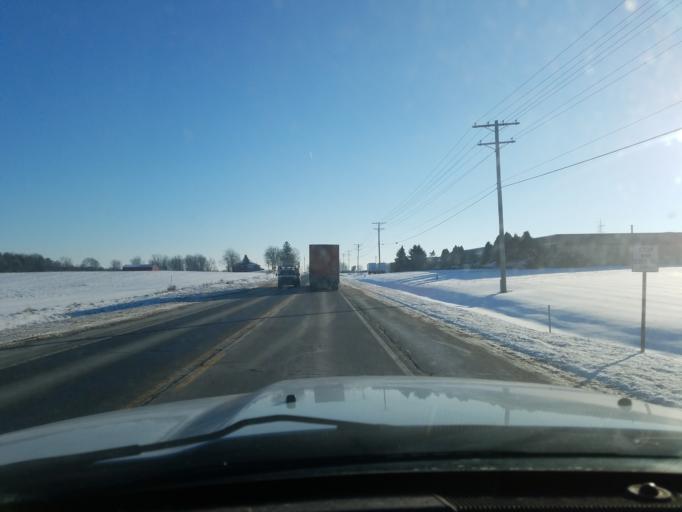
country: US
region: Indiana
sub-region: Noble County
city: Rome City
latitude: 41.4527
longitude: -85.3453
